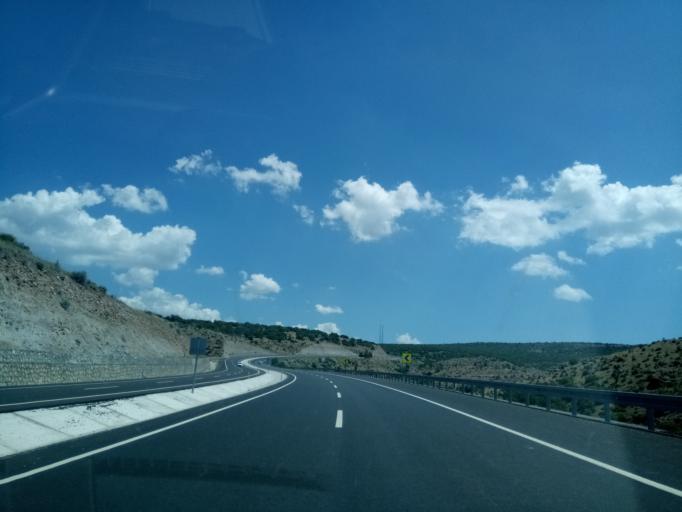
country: TR
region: Konya
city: Cavus
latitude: 37.6477
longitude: 31.9528
